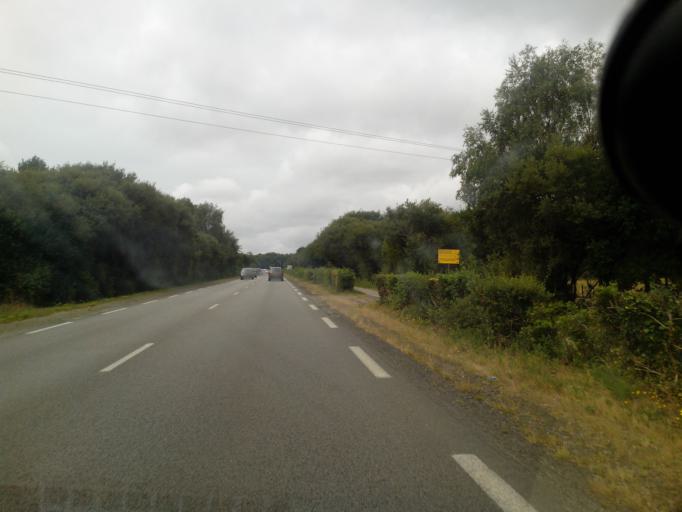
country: FR
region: Brittany
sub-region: Departement du Morbihan
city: Kervignac
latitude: 47.7603
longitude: -3.2749
